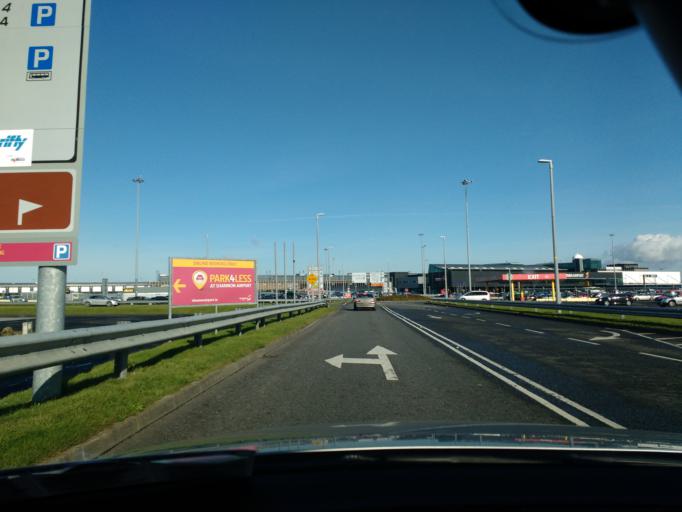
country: IE
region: Munster
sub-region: An Clar
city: Shannon
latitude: 52.6907
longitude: -8.9246
